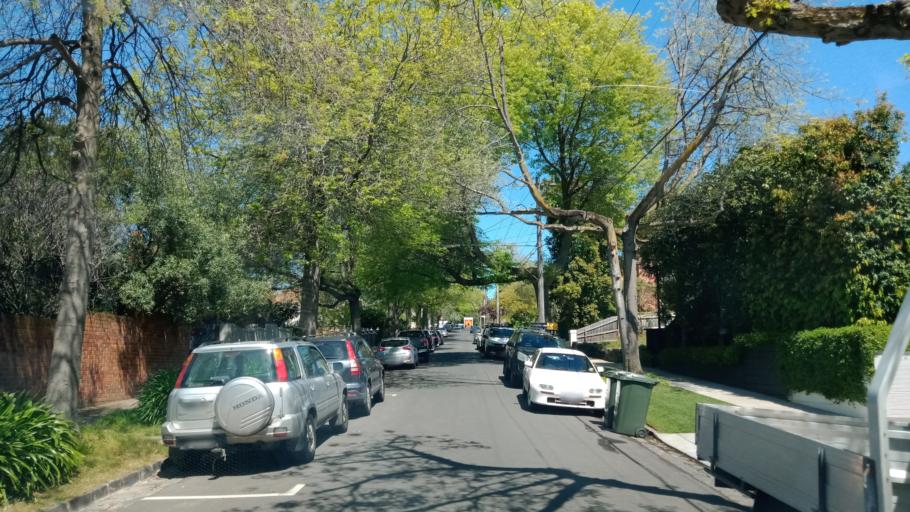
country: AU
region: Victoria
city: Glenferrie
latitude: -37.8426
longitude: 145.0359
